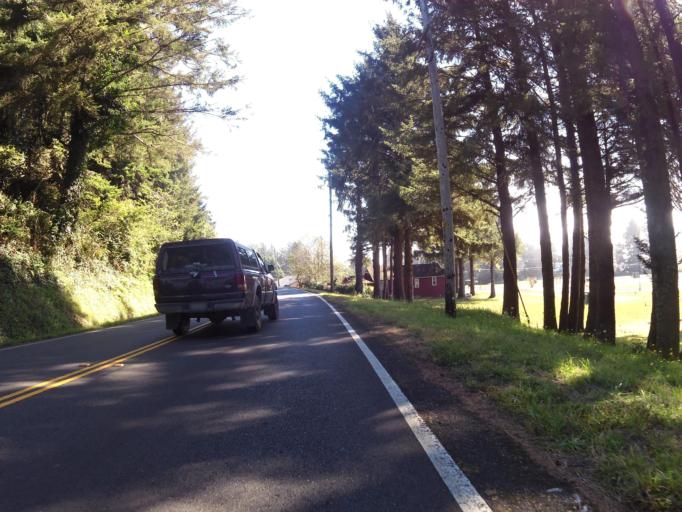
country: US
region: Oregon
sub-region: Curry County
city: Harbor
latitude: 41.9532
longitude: -124.2021
